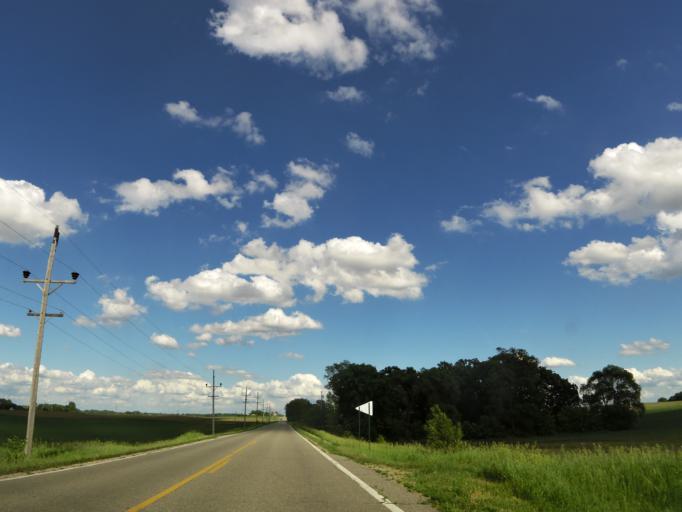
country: US
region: Minnesota
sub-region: Meeker County
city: Dassel
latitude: 45.0664
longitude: -94.2863
